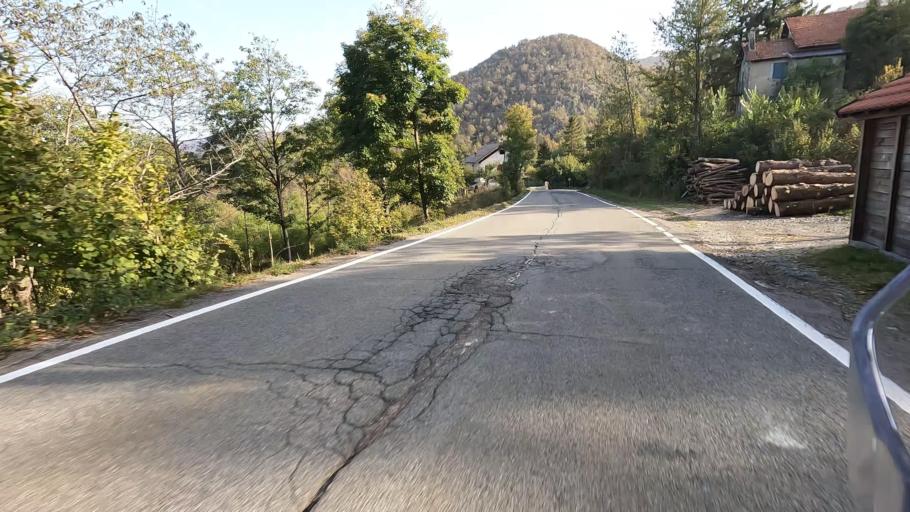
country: IT
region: Liguria
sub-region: Provincia di Savona
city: Urbe
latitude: 44.4598
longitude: 8.5544
